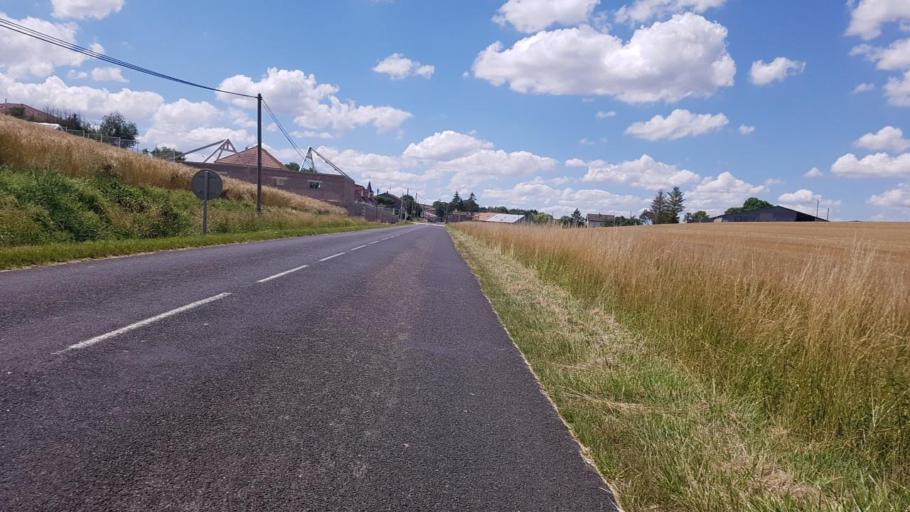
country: FR
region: Lorraine
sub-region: Departement de la Meuse
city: Vacon
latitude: 48.6652
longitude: 5.5523
